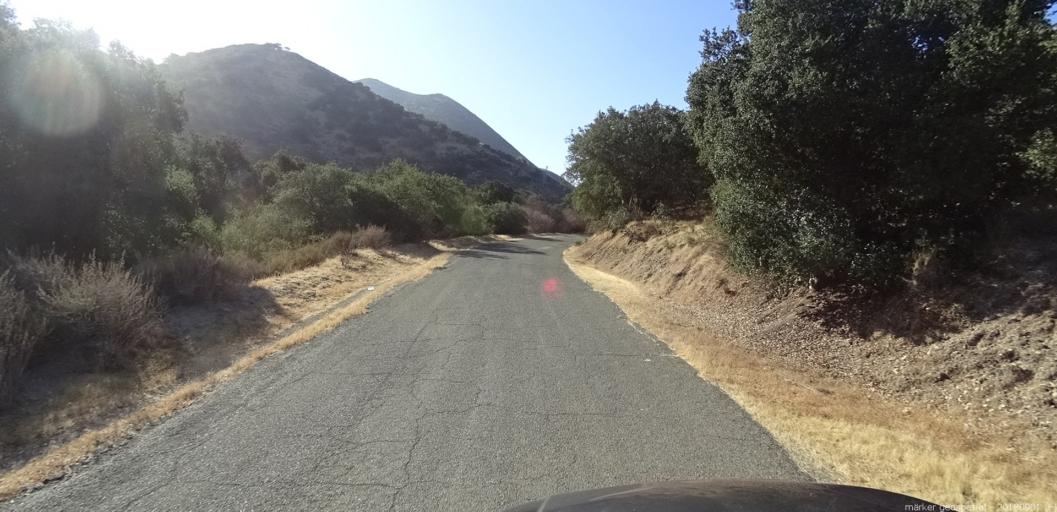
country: US
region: California
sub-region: Monterey County
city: Greenfield
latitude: 36.2322
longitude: -121.2828
